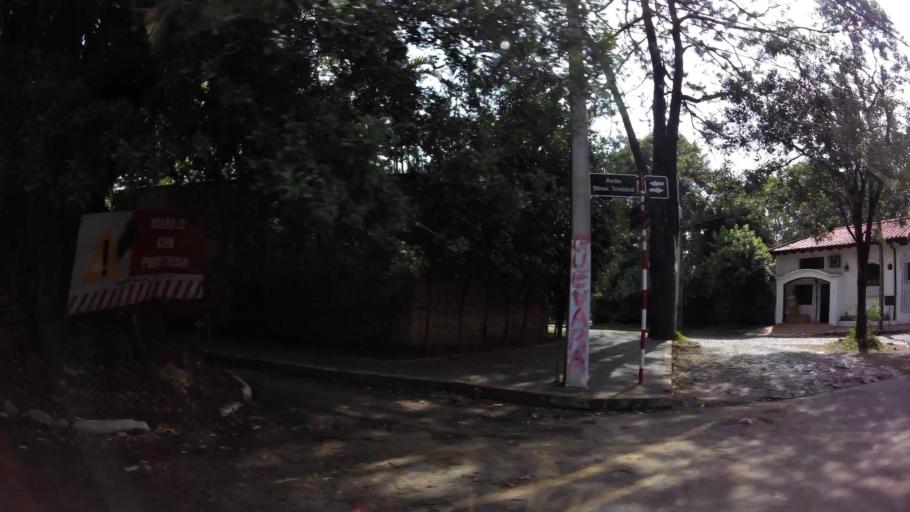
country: PY
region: Asuncion
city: Asuncion
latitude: -25.2662
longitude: -57.5686
